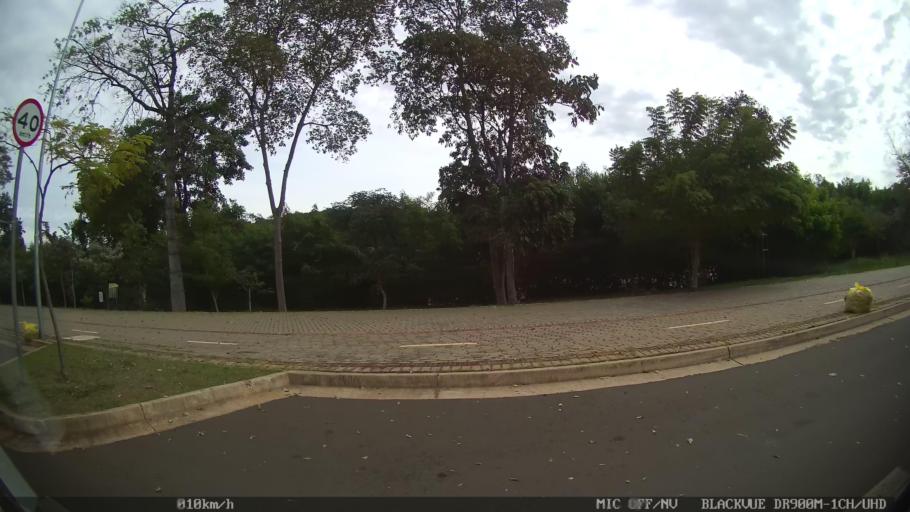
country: BR
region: Sao Paulo
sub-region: Piracicaba
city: Piracicaba
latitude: -22.7080
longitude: -47.6505
